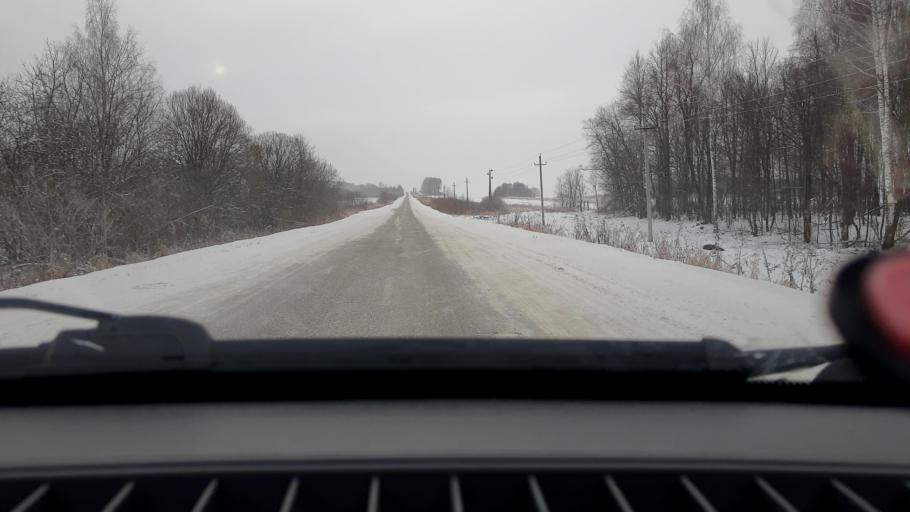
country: RU
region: Bashkortostan
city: Iglino
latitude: 54.6725
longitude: 56.4199
